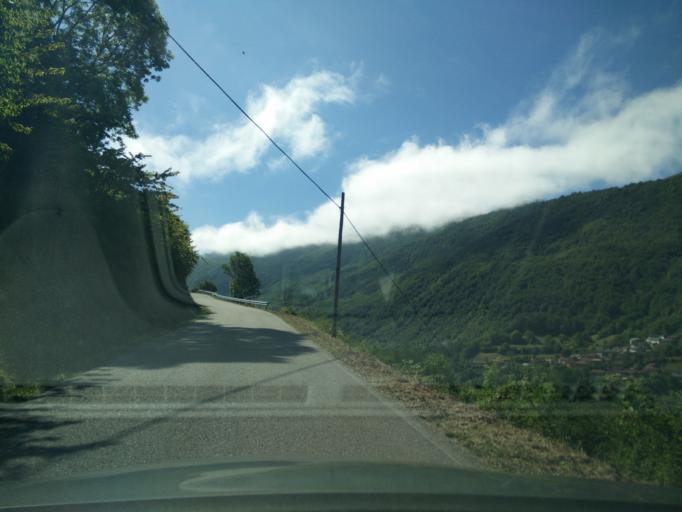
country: ES
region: Asturias
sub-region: Province of Asturias
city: Pola de Somiedo
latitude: 43.0853
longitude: -6.2363
